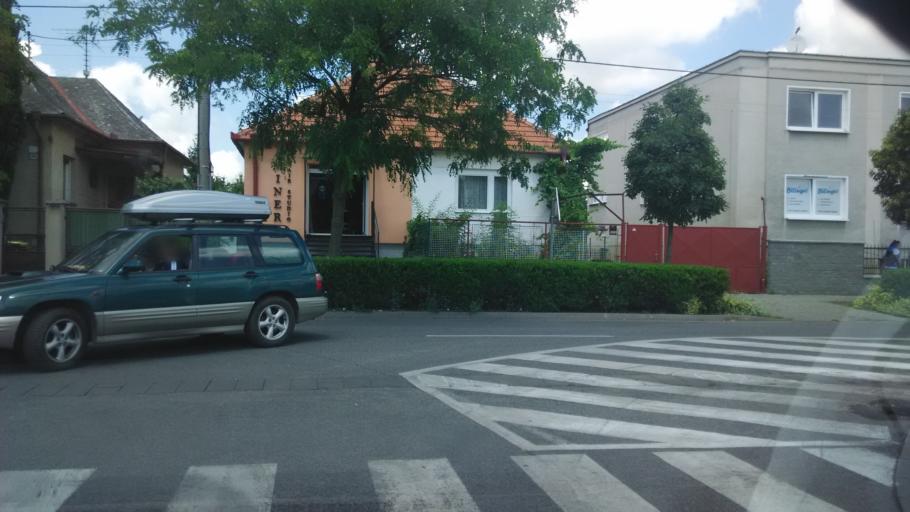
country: SK
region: Trnavsky
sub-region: Okres Trnava
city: Trnava
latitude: 48.3705
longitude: 17.5791
